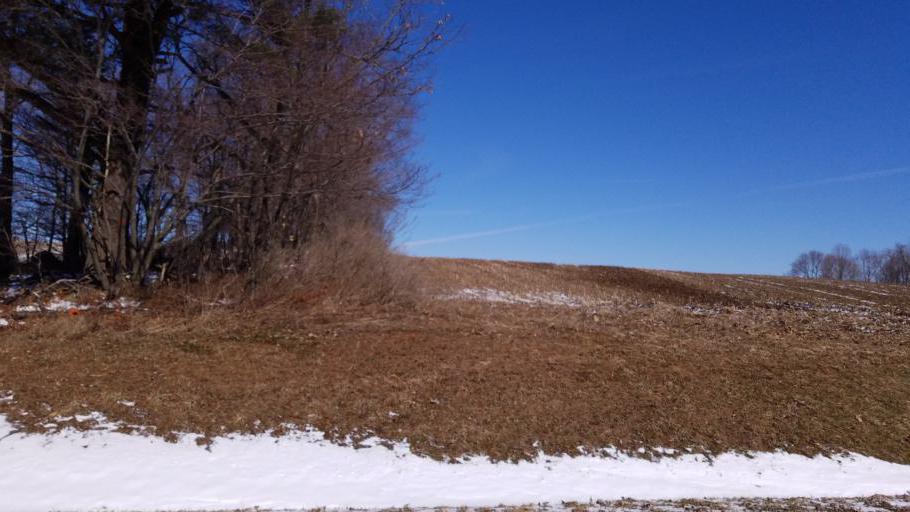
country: US
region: New York
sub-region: Allegany County
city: Andover
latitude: 42.0607
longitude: -77.7965
